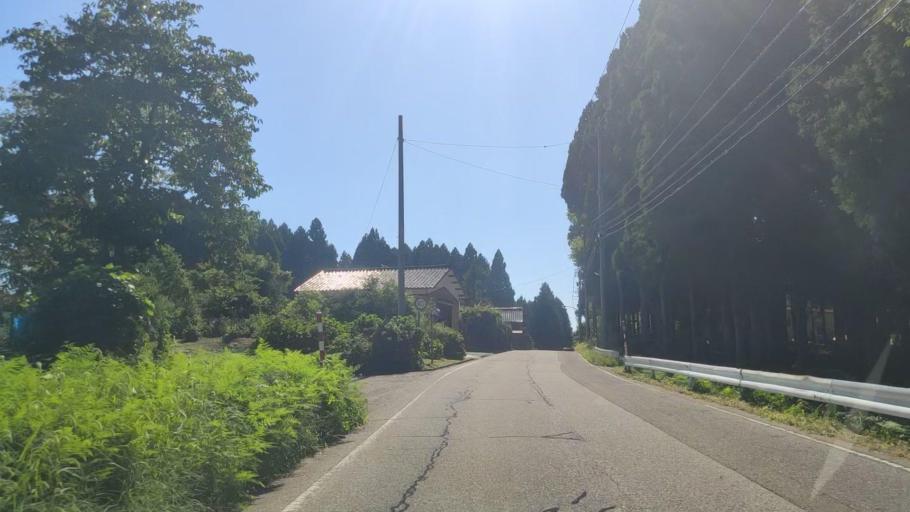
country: JP
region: Ishikawa
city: Nanao
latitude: 37.4624
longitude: 137.3065
